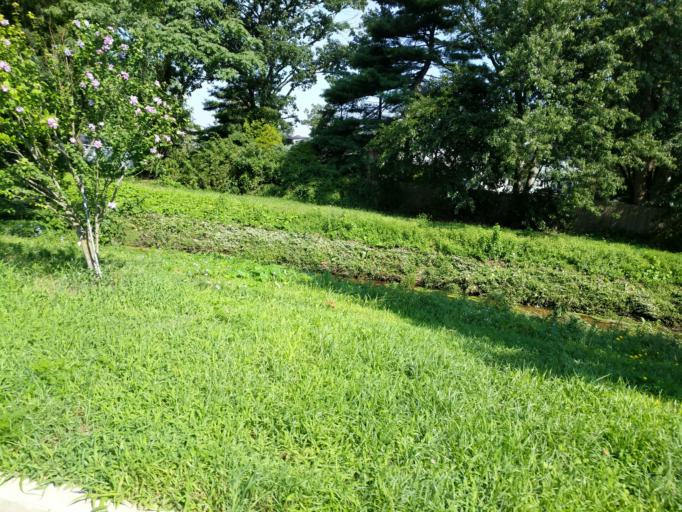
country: US
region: New York
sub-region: Nassau County
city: Hewlett
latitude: 40.6522
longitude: -73.7035
